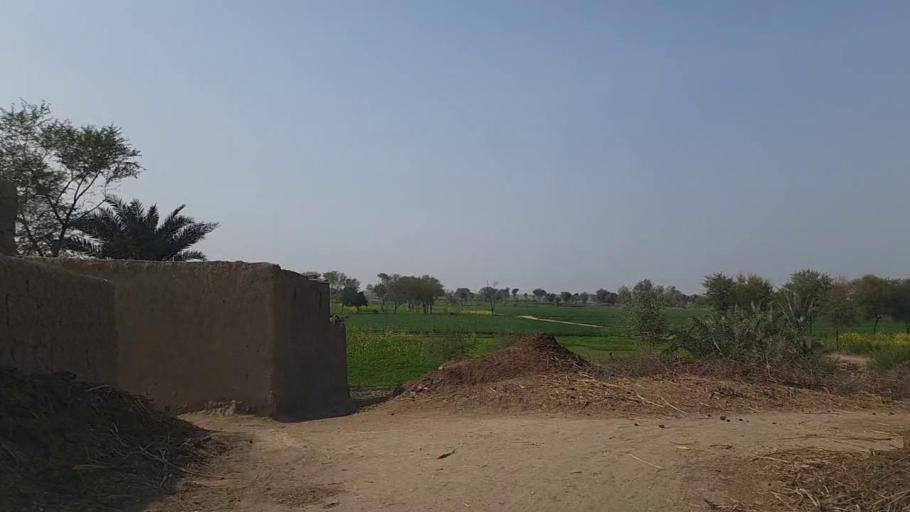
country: PK
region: Sindh
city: Daur
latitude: 26.4903
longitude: 68.4401
